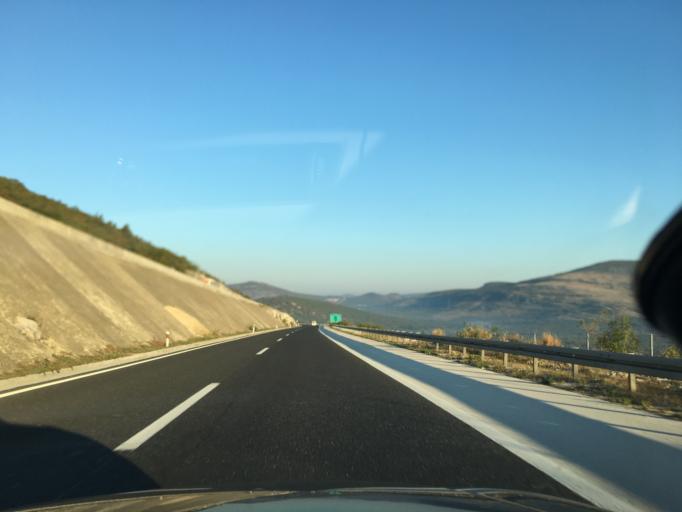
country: HR
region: Splitsko-Dalmatinska
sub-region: Grad Trogir
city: Trogir
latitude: 43.6279
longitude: 16.2338
